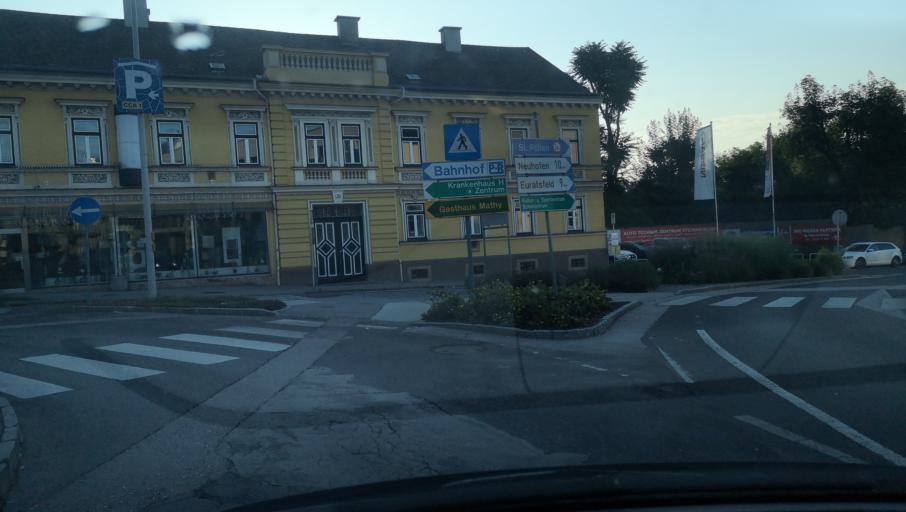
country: AT
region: Lower Austria
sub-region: Politischer Bezirk Amstetten
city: Amstetten
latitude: 48.1217
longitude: 14.8697
